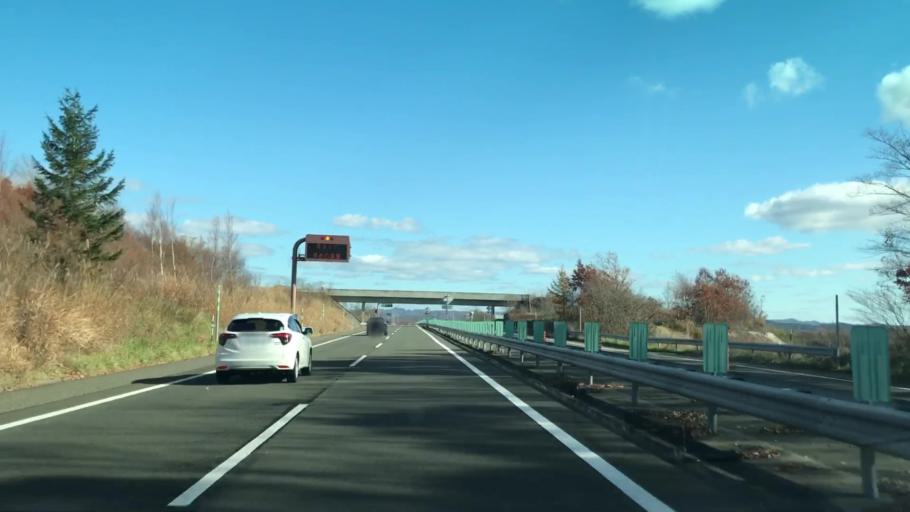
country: JP
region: Hokkaido
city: Chitose
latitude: 42.8930
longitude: 141.8080
